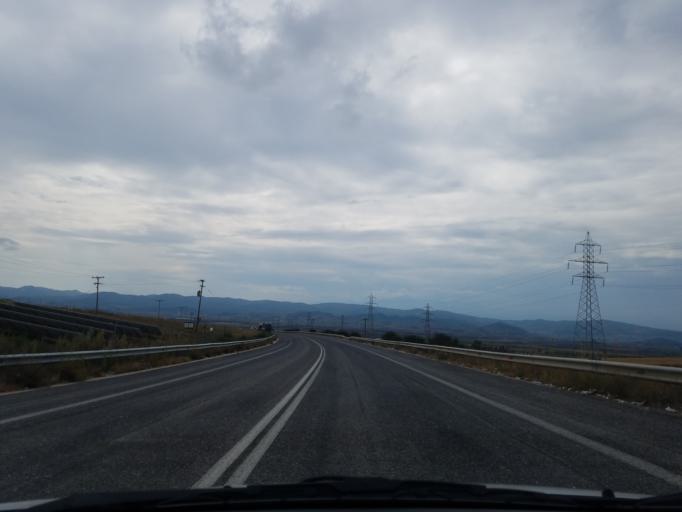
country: GR
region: Central Greece
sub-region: Nomos Fthiotidos
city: Domokos
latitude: 39.0946
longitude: 22.3046
